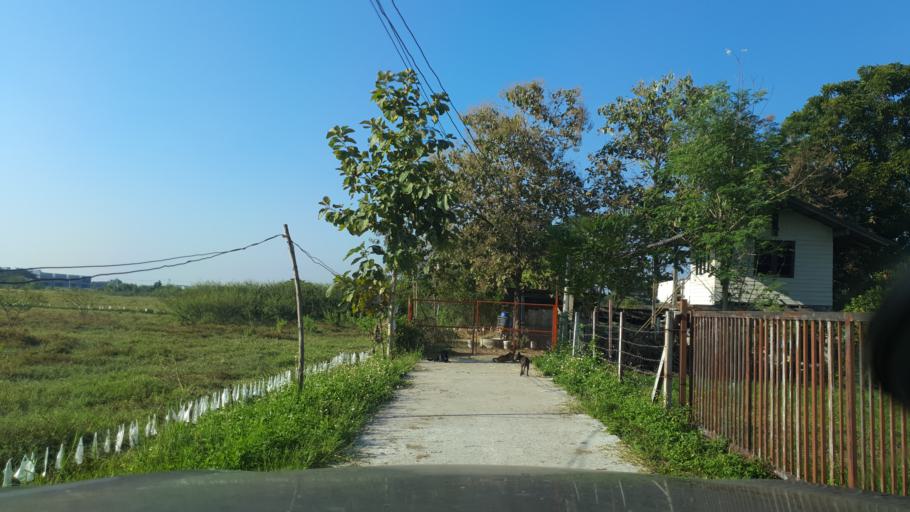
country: TH
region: Chiang Mai
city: San Kamphaeng
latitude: 18.7127
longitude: 99.1439
